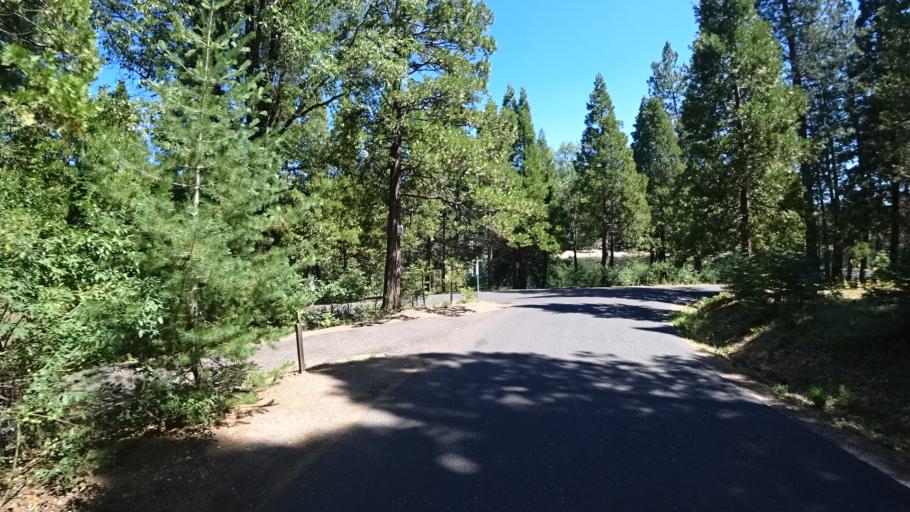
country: US
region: California
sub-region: Calaveras County
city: Arnold
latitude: 38.2334
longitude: -120.3757
